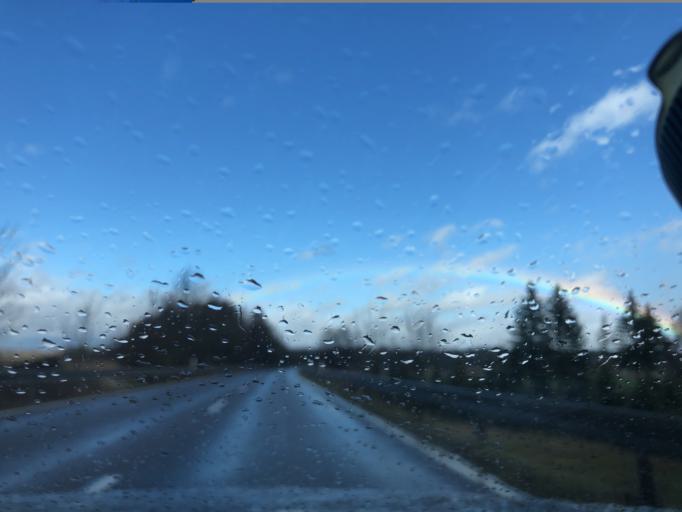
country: DE
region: Bavaria
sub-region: Upper Bavaria
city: Buxheim
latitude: 48.7795
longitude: 11.3220
